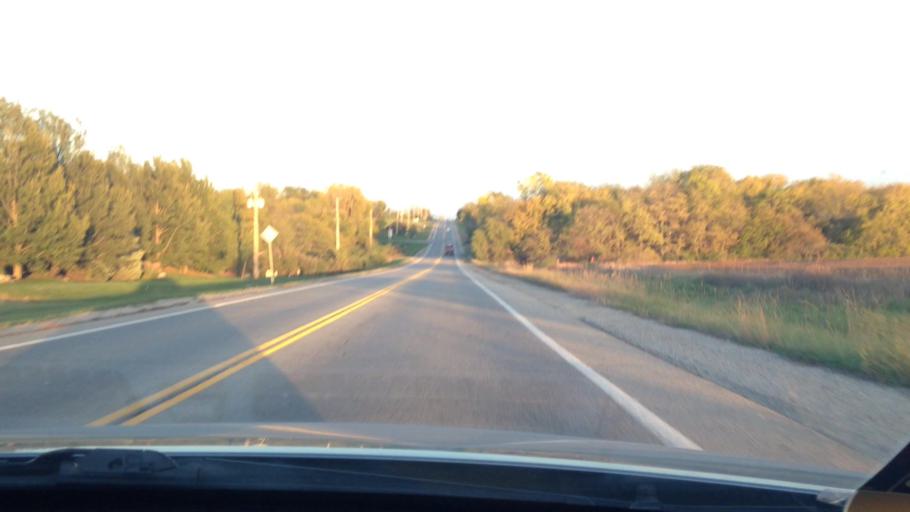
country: US
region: Kansas
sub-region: Johnson County
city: Gardner
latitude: 38.8545
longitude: -94.8852
